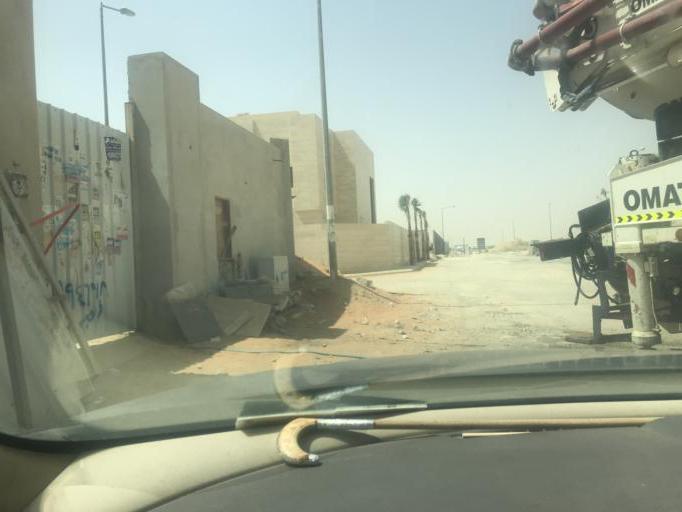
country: SA
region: Ar Riyad
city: Riyadh
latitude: 24.7864
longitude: 46.5822
